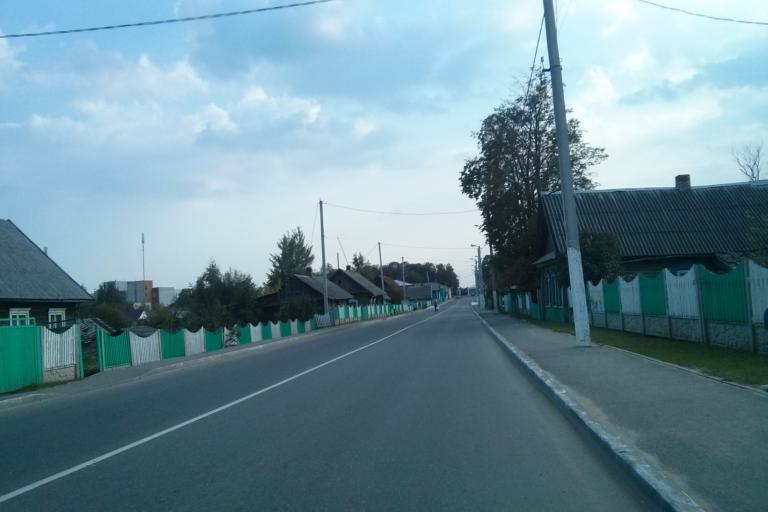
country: BY
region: Minsk
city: Chervyen'
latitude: 53.7180
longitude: 28.4179
